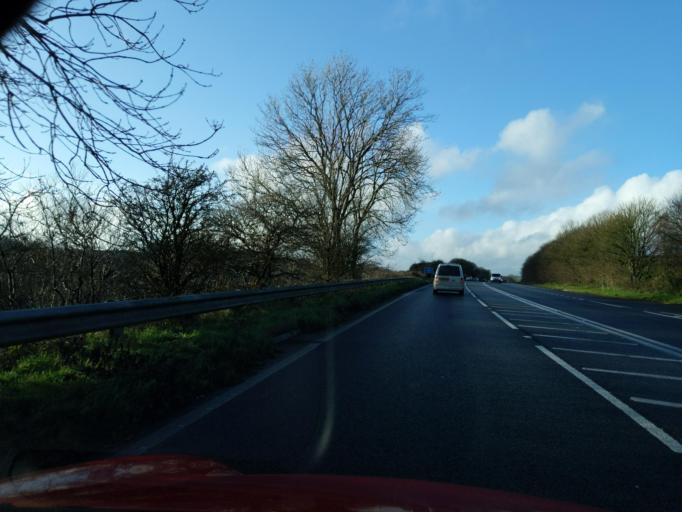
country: GB
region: England
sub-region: Cornwall
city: Pillaton
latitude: 50.4104
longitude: -4.3651
